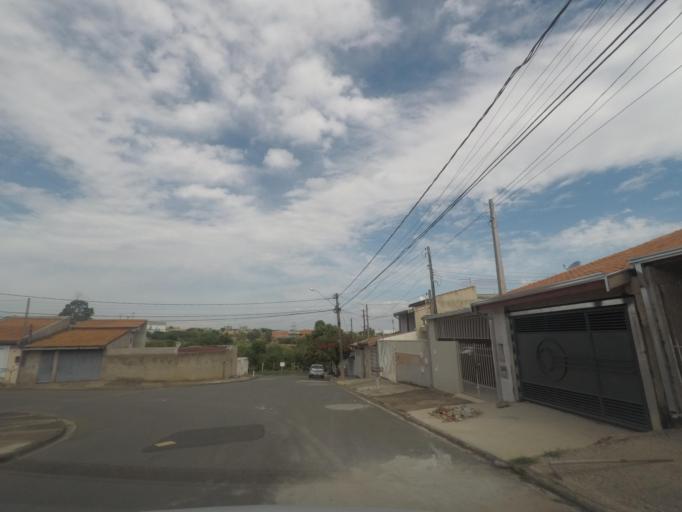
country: BR
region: Sao Paulo
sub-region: Sumare
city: Sumare
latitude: -22.8085
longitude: -47.2638
